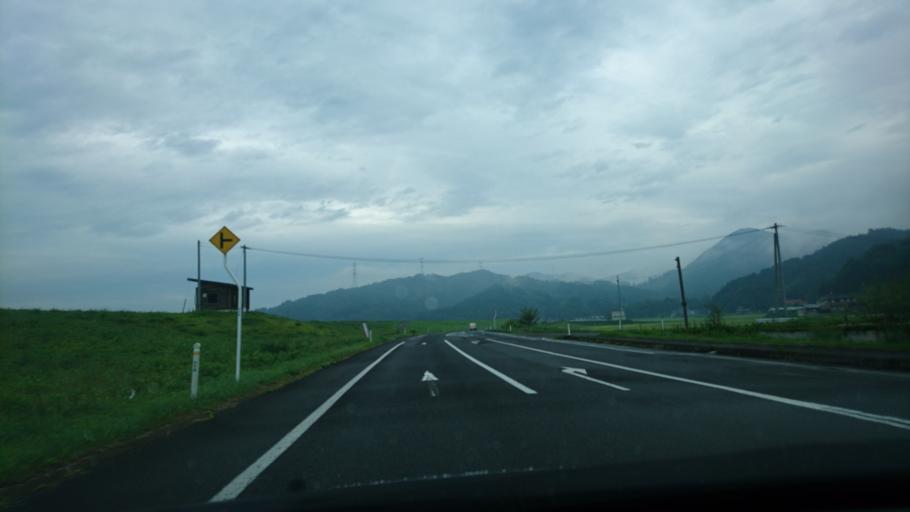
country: JP
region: Iwate
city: Ichinoseki
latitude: 38.9219
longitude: 141.2558
